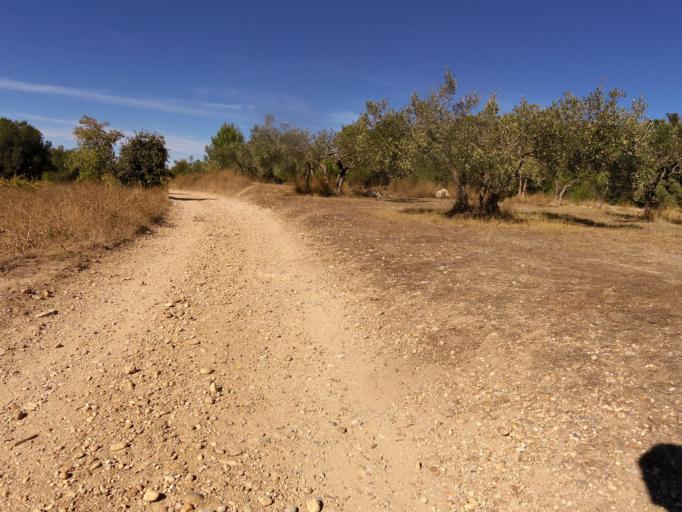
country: FR
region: Languedoc-Roussillon
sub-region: Departement du Gard
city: Mus
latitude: 43.7454
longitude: 4.1979
